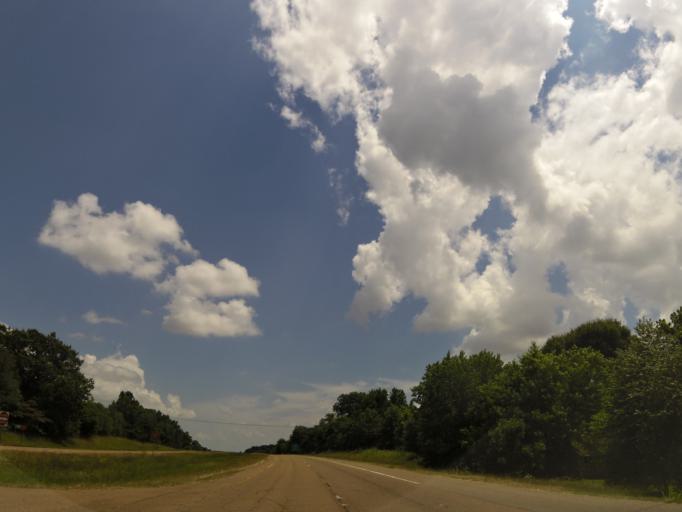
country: US
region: Tennessee
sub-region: Dyer County
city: Dyersburg
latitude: 35.9764
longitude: -89.3407
